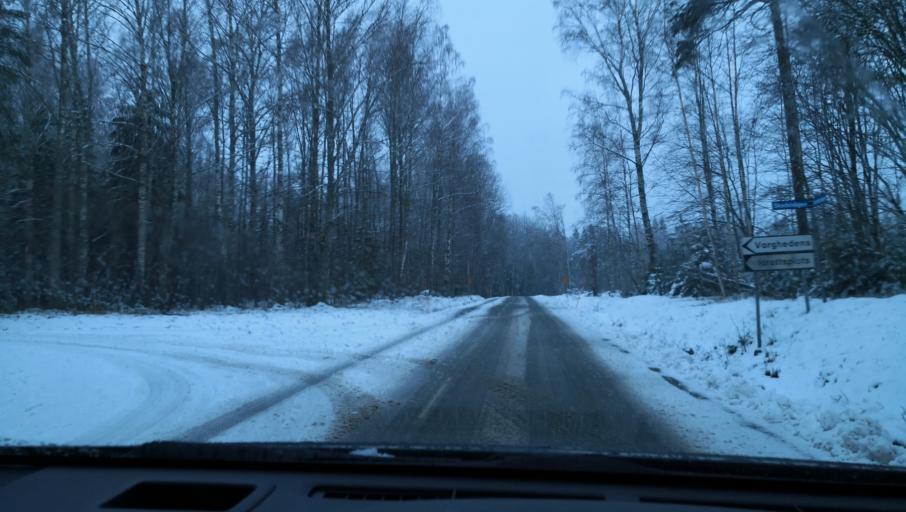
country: SE
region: Vaestmanland
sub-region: Kopings Kommun
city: Kolsva
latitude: 59.5968
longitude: 15.8261
